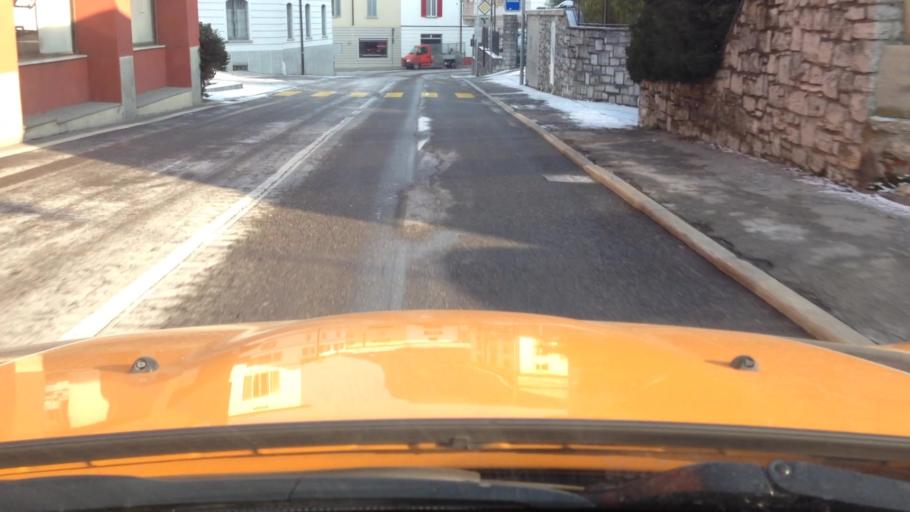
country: CH
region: Ticino
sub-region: Mendrisio District
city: Mendrisio
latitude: 45.8683
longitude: 8.9848
